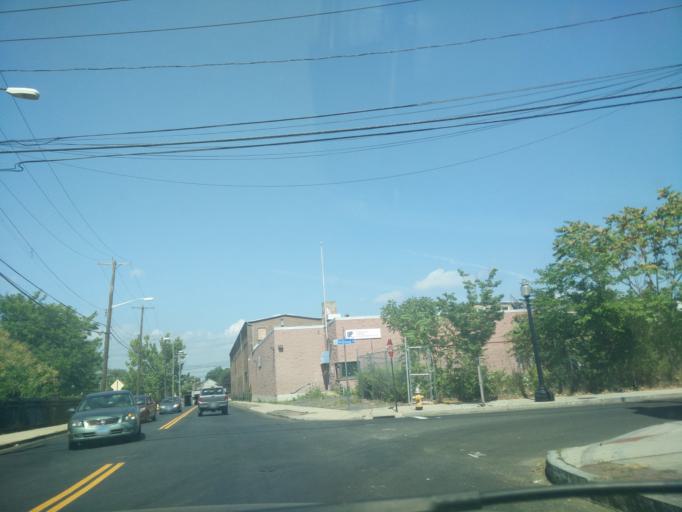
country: US
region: Connecticut
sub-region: Fairfield County
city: Stratford
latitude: 41.1839
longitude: -73.1703
